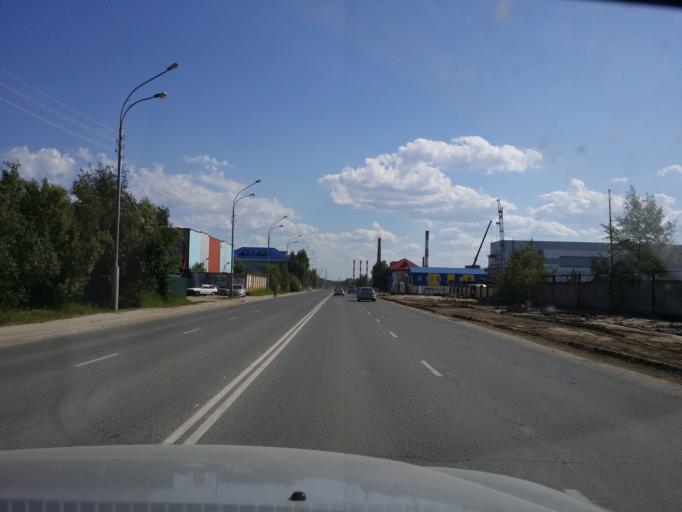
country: RU
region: Khanty-Mansiyskiy Avtonomnyy Okrug
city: Nizhnevartovsk
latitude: 60.9435
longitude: 76.5483
